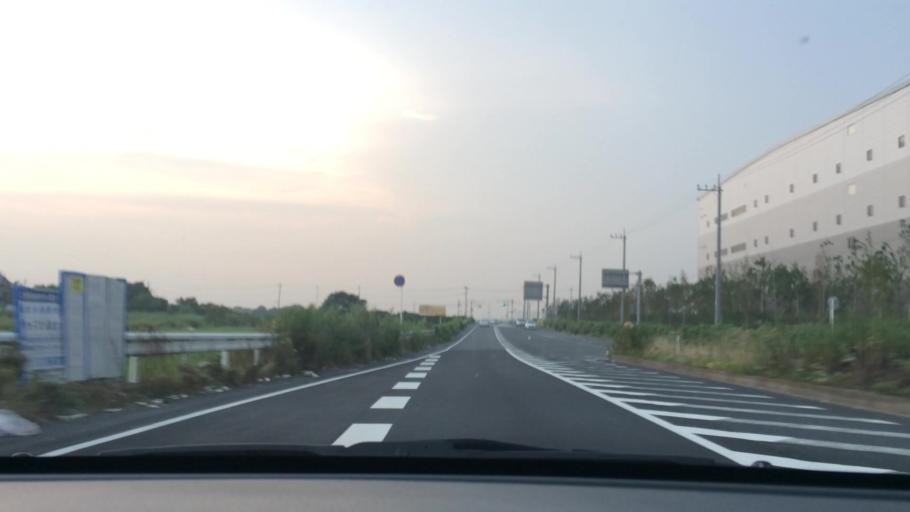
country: JP
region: Chiba
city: Nagareyama
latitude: 35.8859
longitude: 139.8968
